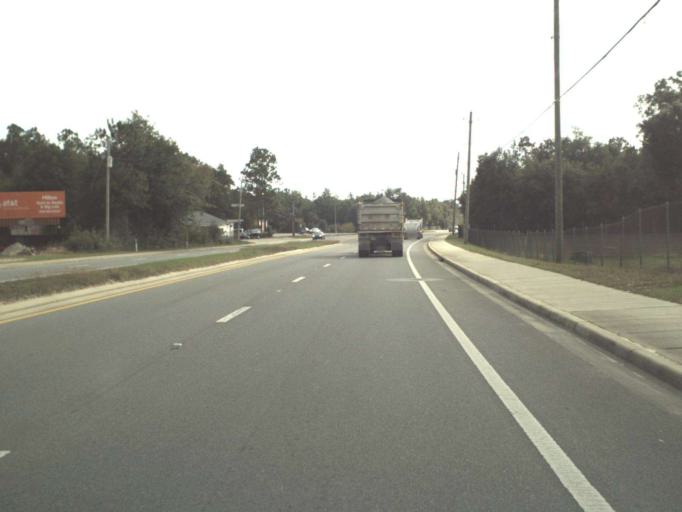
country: US
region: Florida
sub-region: Santa Rosa County
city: Milton
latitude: 30.6567
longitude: -87.0475
